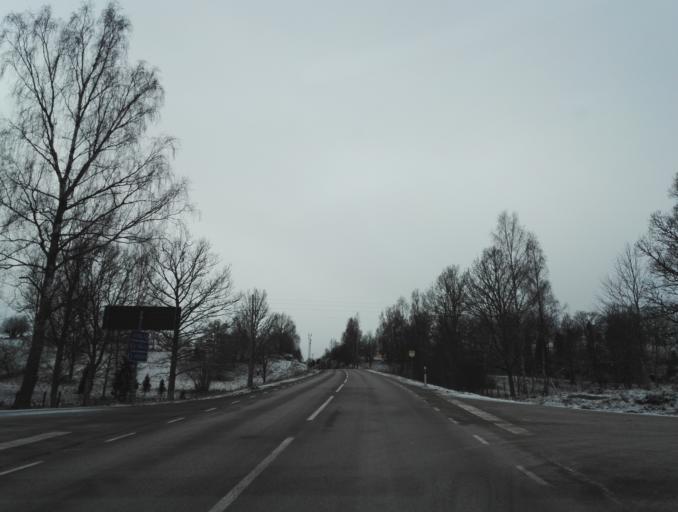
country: SE
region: Kalmar
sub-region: Hultsfreds Kommun
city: Virserum
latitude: 57.2953
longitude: 15.5680
